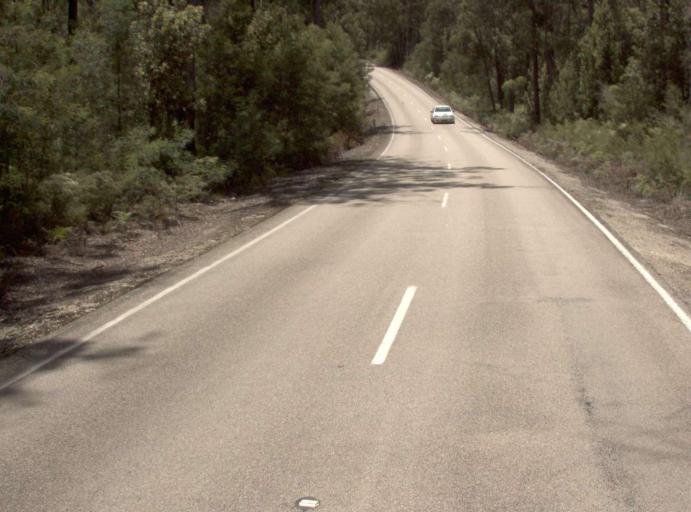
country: AU
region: Victoria
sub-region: East Gippsland
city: Lakes Entrance
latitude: -37.6503
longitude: 147.8916
